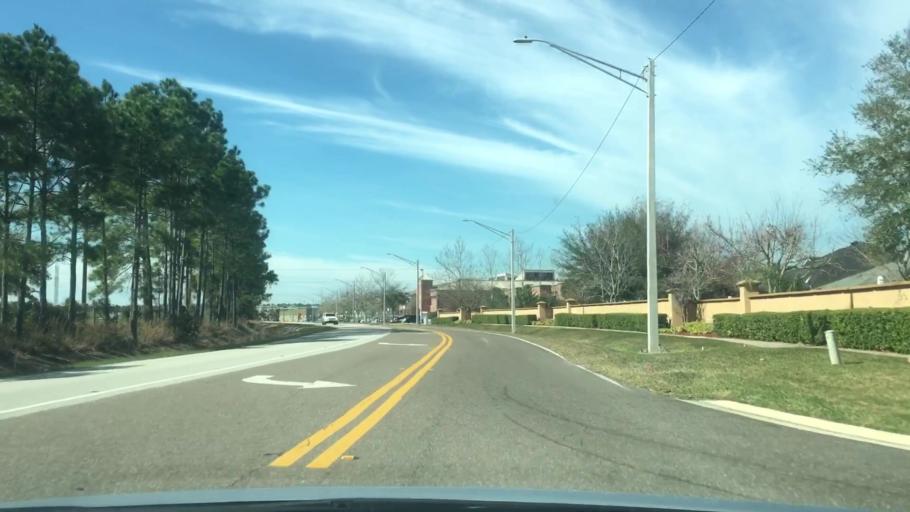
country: US
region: Florida
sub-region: Duval County
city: Atlantic Beach
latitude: 30.3221
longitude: -81.4847
